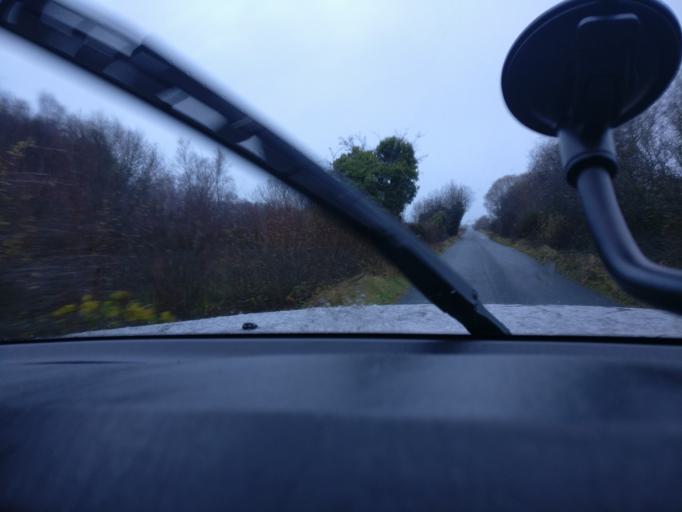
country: IE
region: Connaught
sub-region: County Galway
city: Loughrea
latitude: 53.2345
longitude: -8.5244
